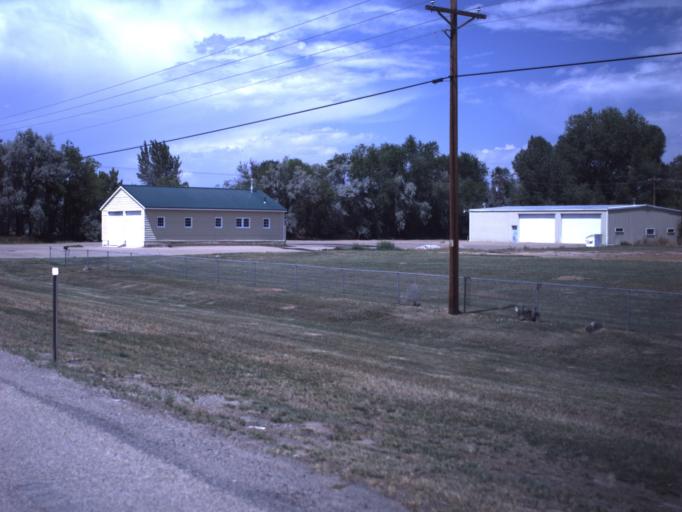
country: US
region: Utah
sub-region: Duchesne County
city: Roosevelt
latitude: 40.3020
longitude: -109.8960
